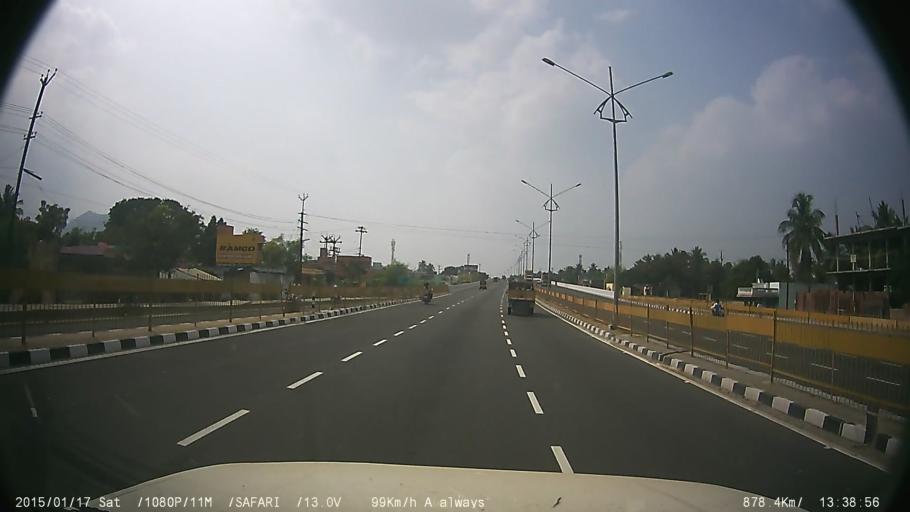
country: IN
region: Tamil Nadu
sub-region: Vellore
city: Katpadi
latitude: 12.9422
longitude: 79.1900
